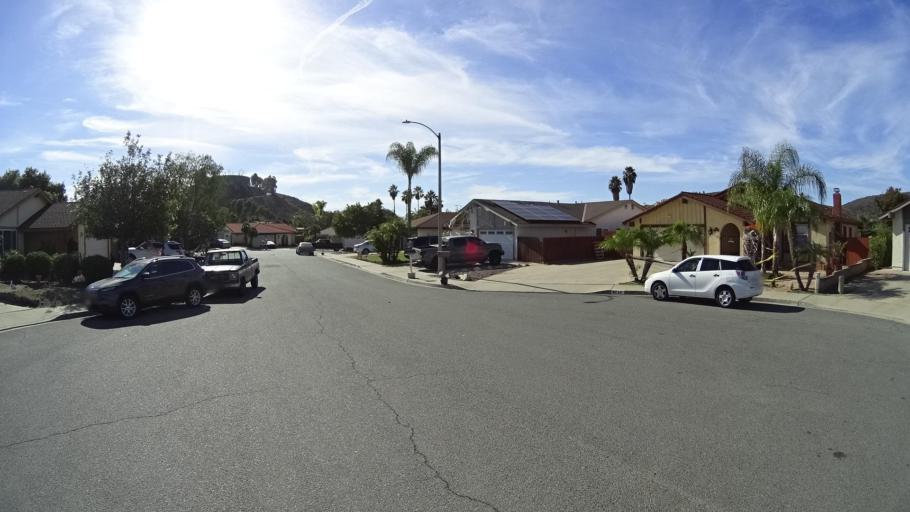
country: US
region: California
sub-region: San Diego County
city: Spring Valley
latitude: 32.7296
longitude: -116.9811
